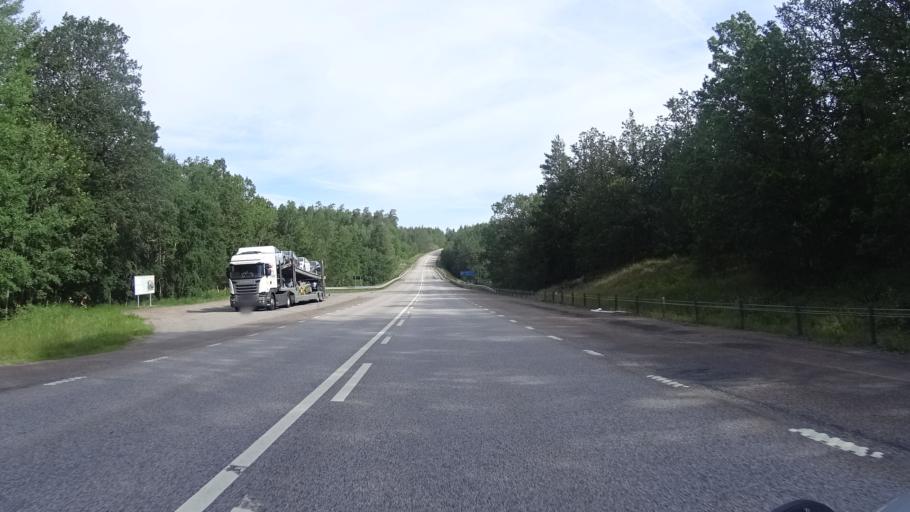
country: SE
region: Kalmar
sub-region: Vasterviks Kommun
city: Ankarsrum
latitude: 57.5487
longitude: 16.4774
